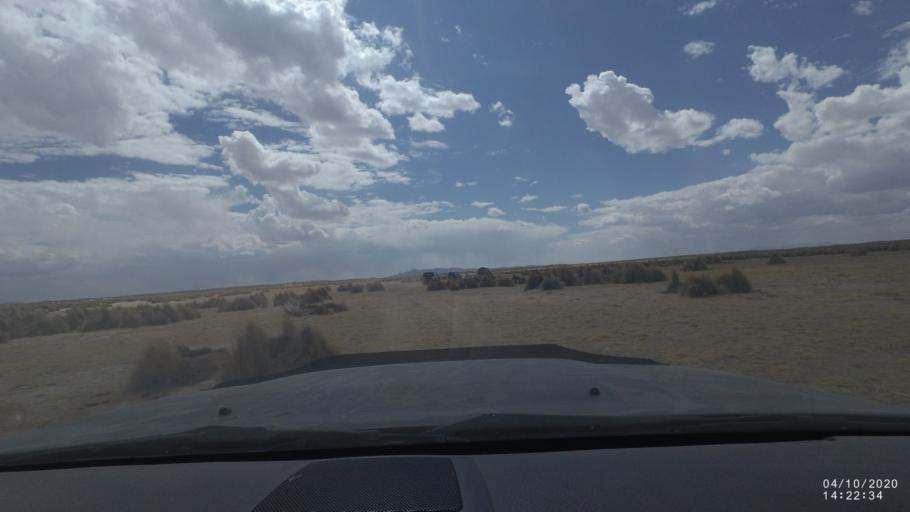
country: BO
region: Oruro
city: Poopo
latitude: -18.6784
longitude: -67.4505
